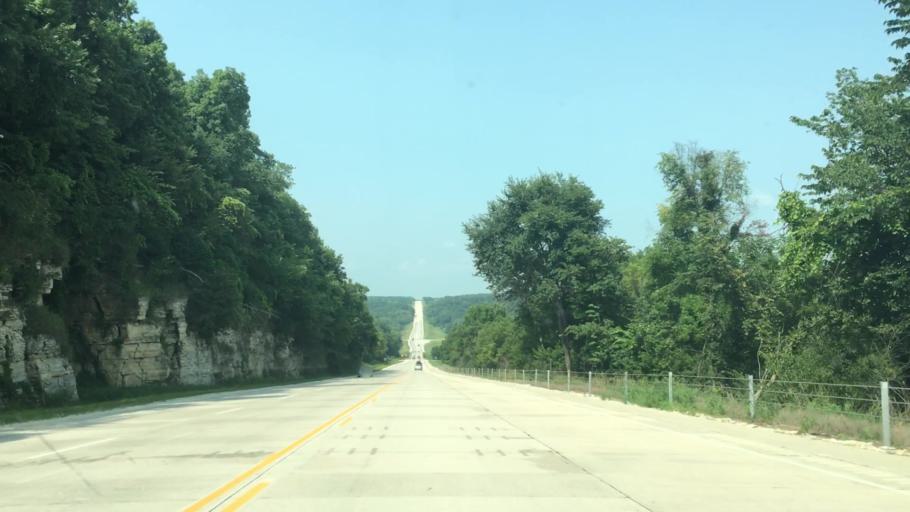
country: US
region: Iowa
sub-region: Winneshiek County
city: Decorah
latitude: 43.3092
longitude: -91.8150
